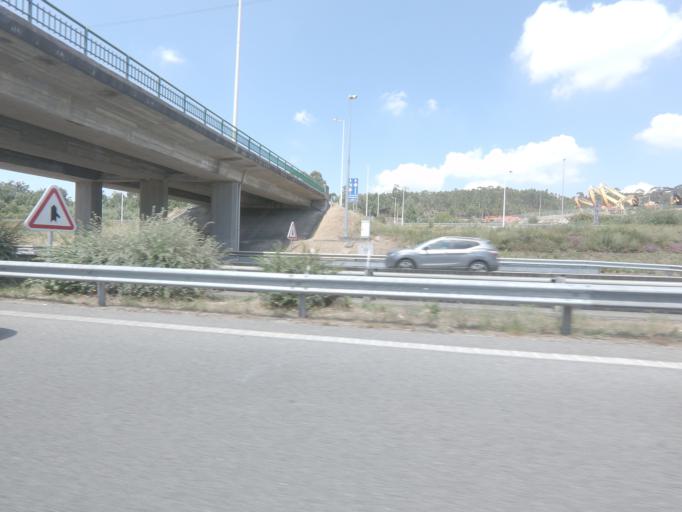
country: PT
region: Porto
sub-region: Paredes
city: Baltar
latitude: 41.1685
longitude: -8.3872
